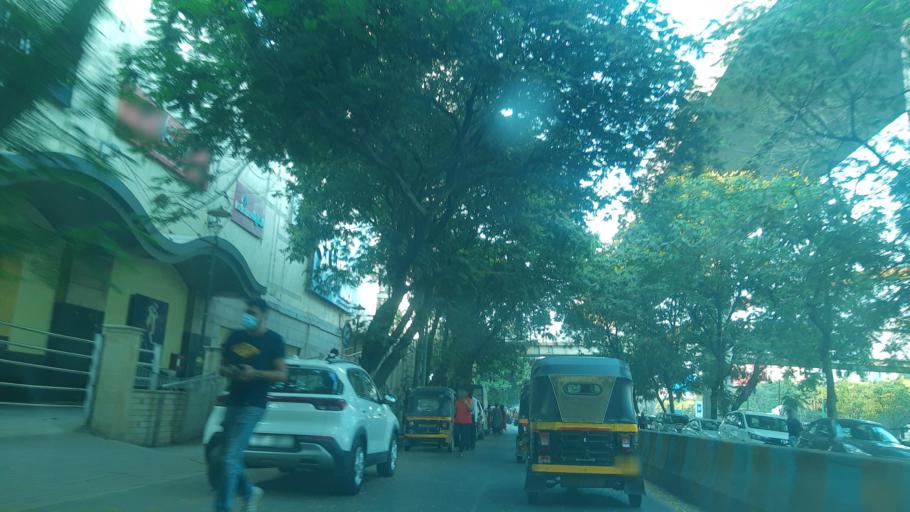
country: IN
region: Maharashtra
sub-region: Thane
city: Thane
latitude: 19.2085
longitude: 72.9722
